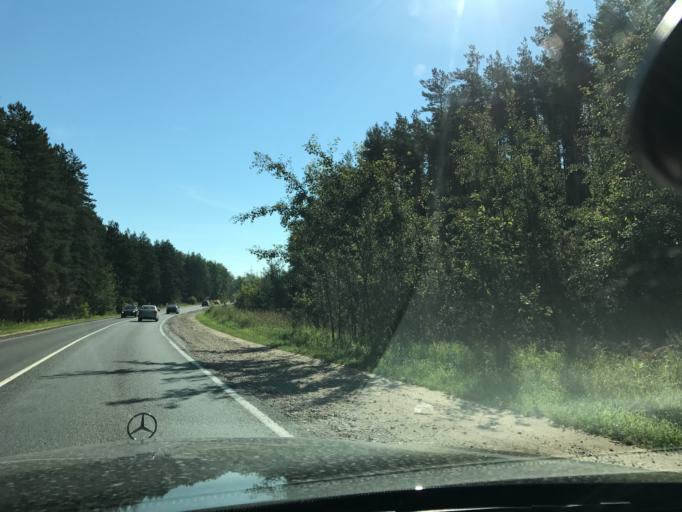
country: RU
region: Vladimir
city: Kirzhach
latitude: 56.1450
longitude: 38.8329
